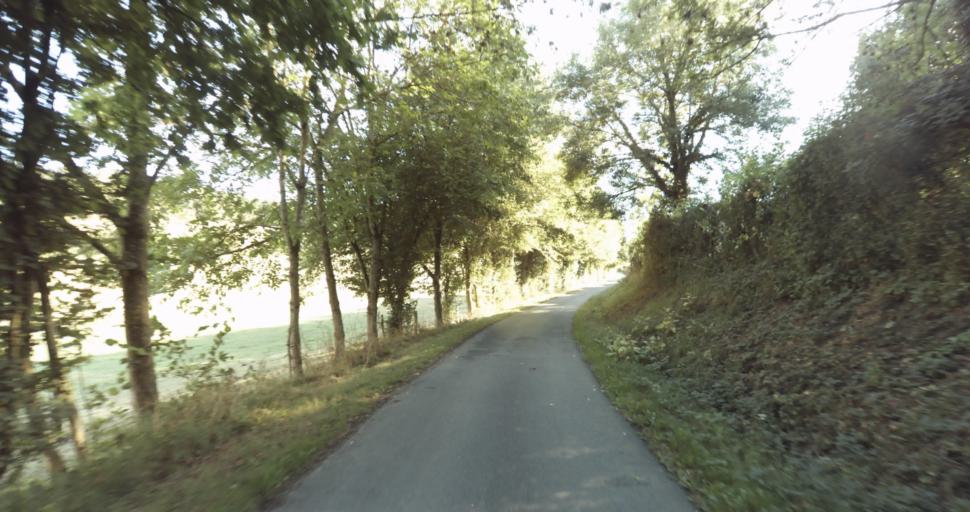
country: FR
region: Lower Normandy
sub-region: Departement de l'Orne
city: Vimoutiers
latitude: 48.9063
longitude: 0.1319
